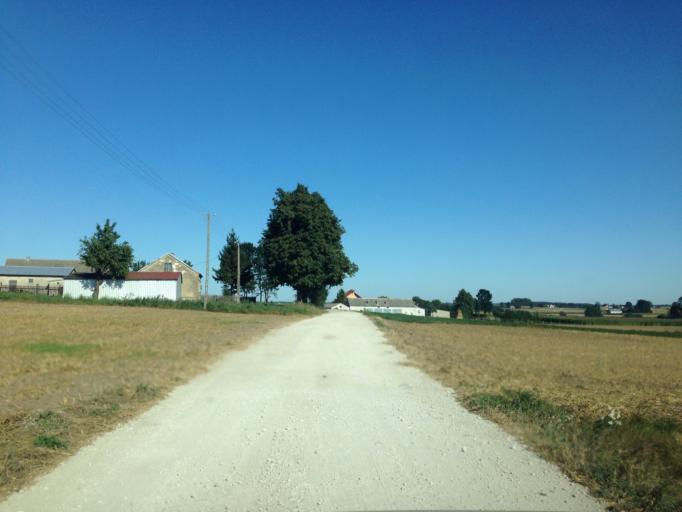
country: PL
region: Kujawsko-Pomorskie
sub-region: Powiat brodnicki
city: Swiedziebnia
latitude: 53.1899
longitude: 19.5724
